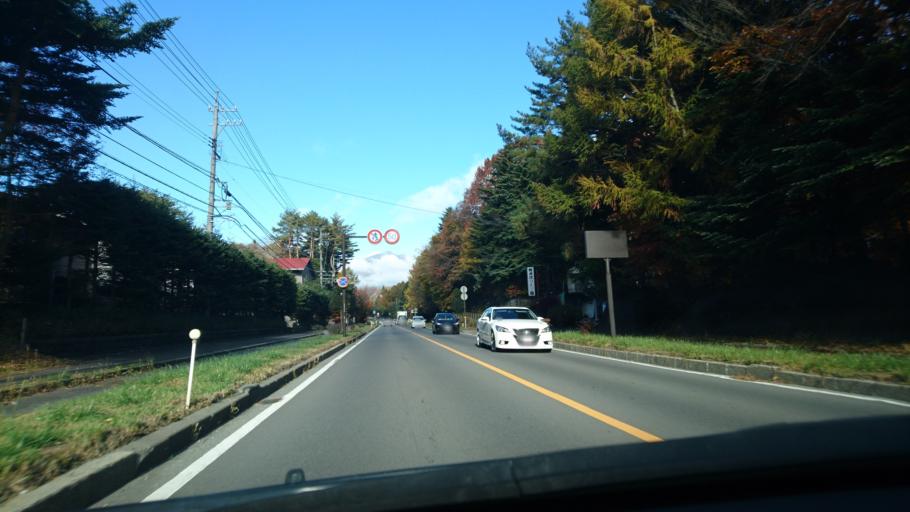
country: JP
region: Nagano
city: Saku
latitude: 36.3285
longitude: 138.6134
